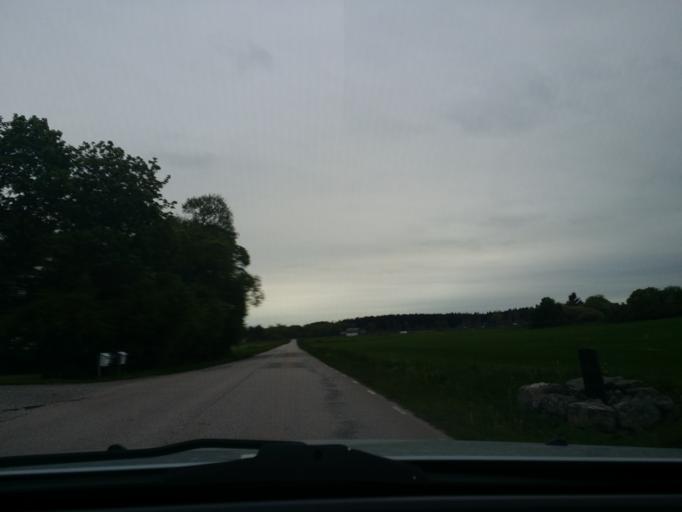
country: SE
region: Vaestmanland
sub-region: Hallstahammars Kommun
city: Kolback
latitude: 59.5365
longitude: 16.3001
